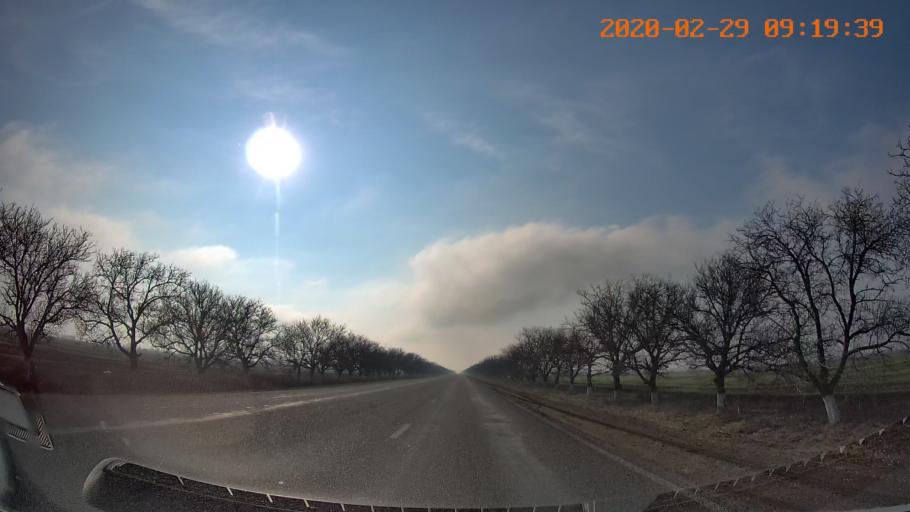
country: MD
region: Telenesti
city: Pervomaisc
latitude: 46.7599
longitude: 29.9411
